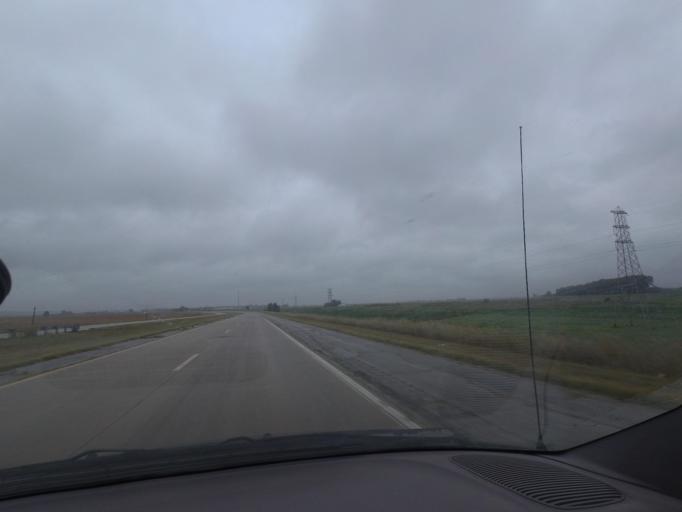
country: US
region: Illinois
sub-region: Adams County
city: Payson
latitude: 39.7270
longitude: -91.2310
